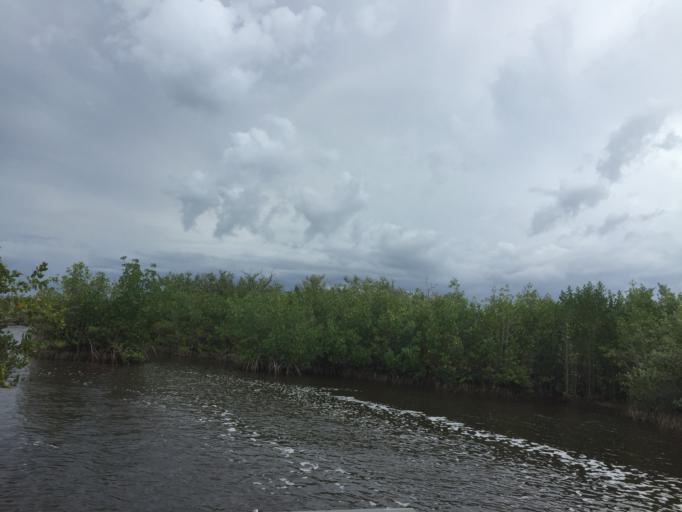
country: US
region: Florida
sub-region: Collier County
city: Marco
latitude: 25.9053
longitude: -81.3688
